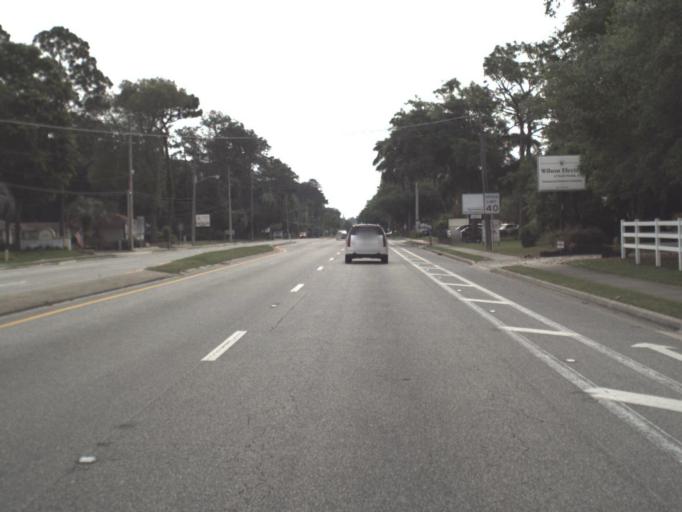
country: US
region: Florida
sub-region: Clay County
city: Orange Park
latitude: 30.1652
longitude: -81.7207
